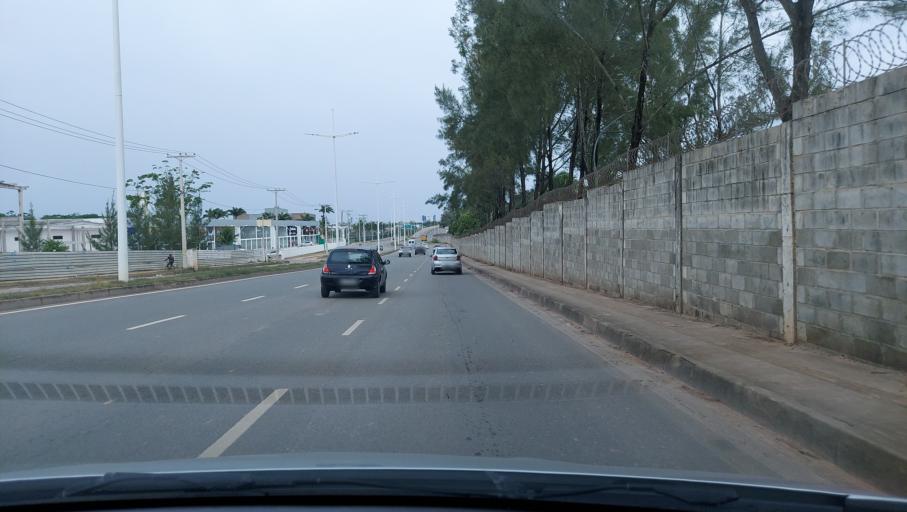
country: BR
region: Bahia
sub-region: Lauro De Freitas
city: Lauro de Freitas
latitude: -12.9425
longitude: -38.3860
